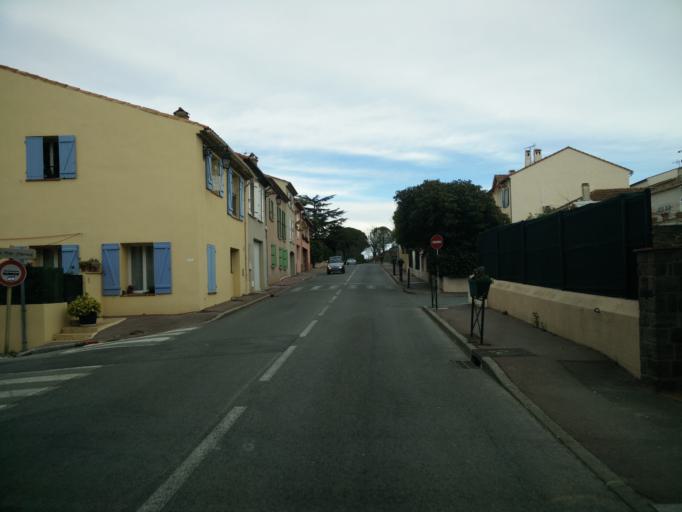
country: FR
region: Provence-Alpes-Cote d'Azur
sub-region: Departement du Var
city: Roquebrune-sur-Argens
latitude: 43.4444
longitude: 6.6412
